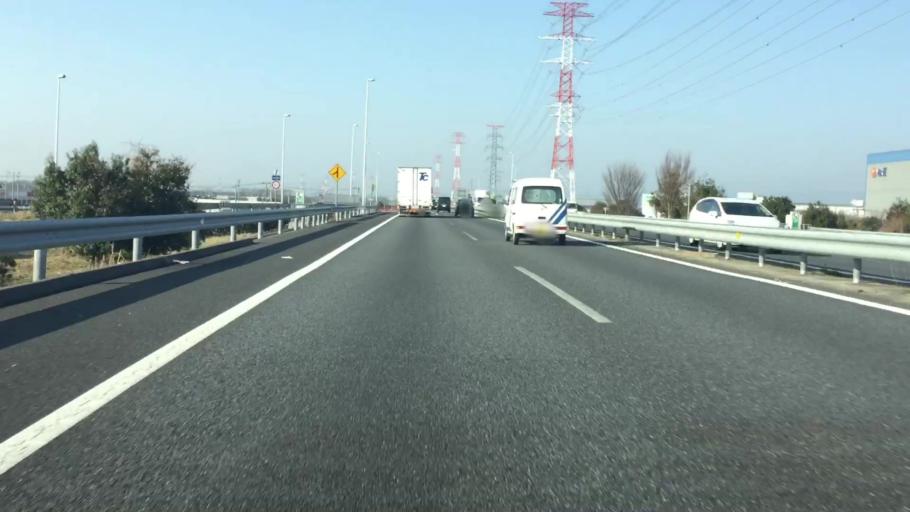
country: JP
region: Saitama
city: Kawagoe
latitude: 35.9820
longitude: 139.4672
